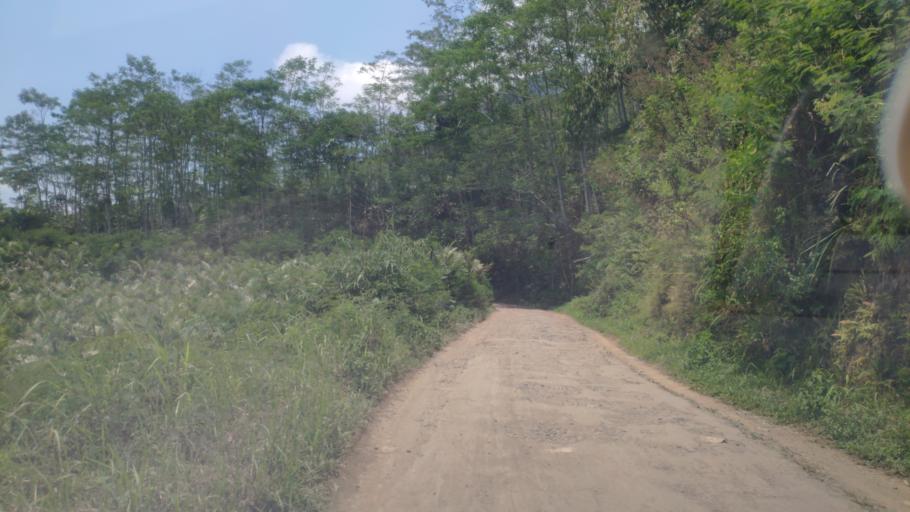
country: ID
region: Central Java
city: Wonosobo
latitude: -7.2810
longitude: 109.7371
